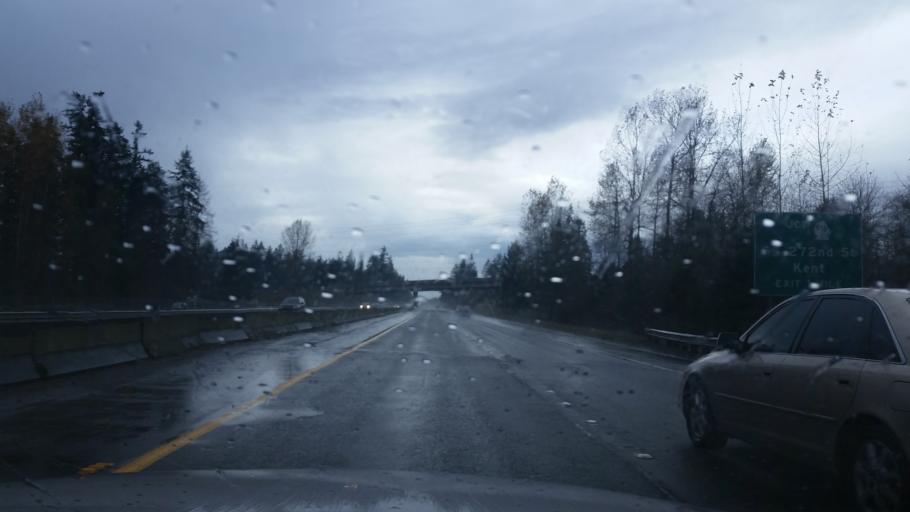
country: US
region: Washington
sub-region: King County
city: Covington
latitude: 47.3692
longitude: -122.0994
